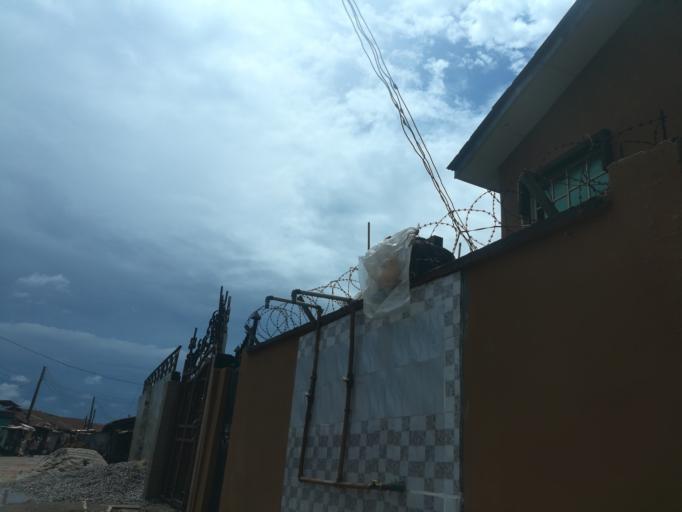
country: NG
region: Lagos
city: Agege
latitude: 6.6154
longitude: 3.3297
